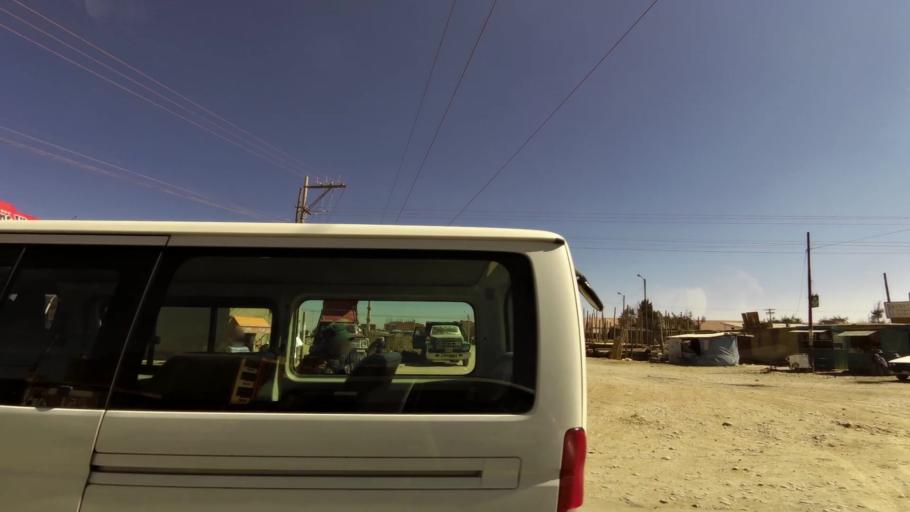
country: BO
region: La Paz
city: La Paz
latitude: -16.5551
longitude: -68.2097
